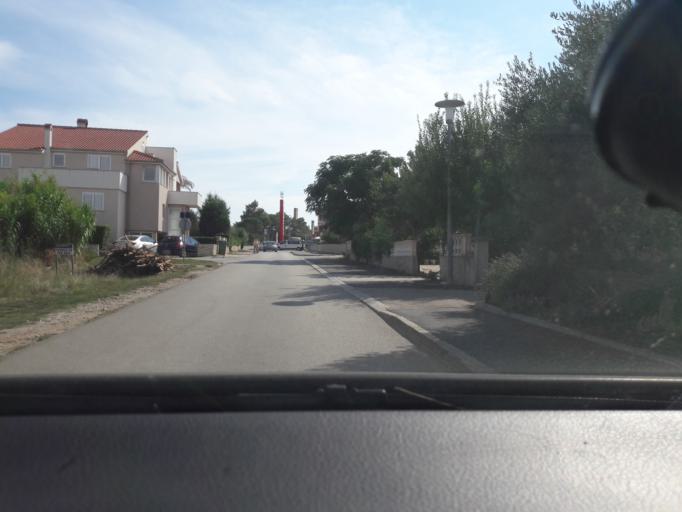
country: HR
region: Zadarska
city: Nin
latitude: 44.2431
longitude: 15.1731
